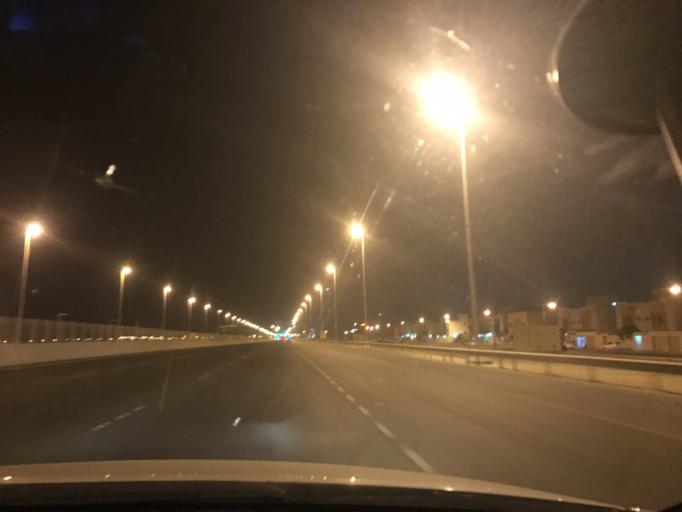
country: BH
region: Muharraq
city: Al Muharraq
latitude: 26.2872
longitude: 50.6381
